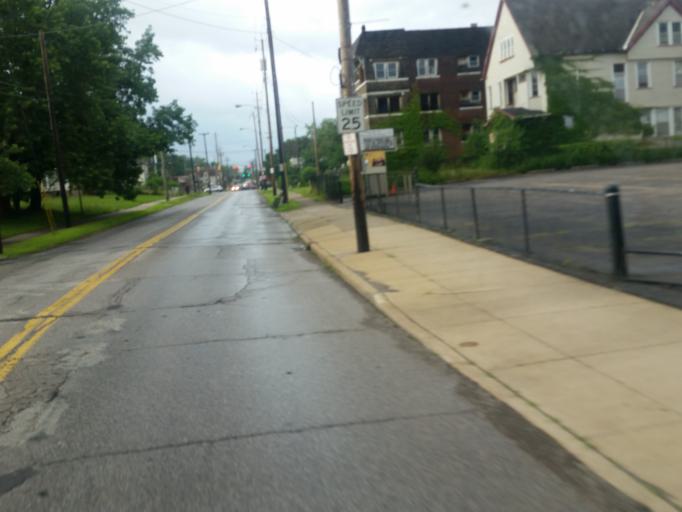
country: US
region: Ohio
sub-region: Cuyahoga County
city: Bratenahl
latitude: 41.5031
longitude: -81.6336
